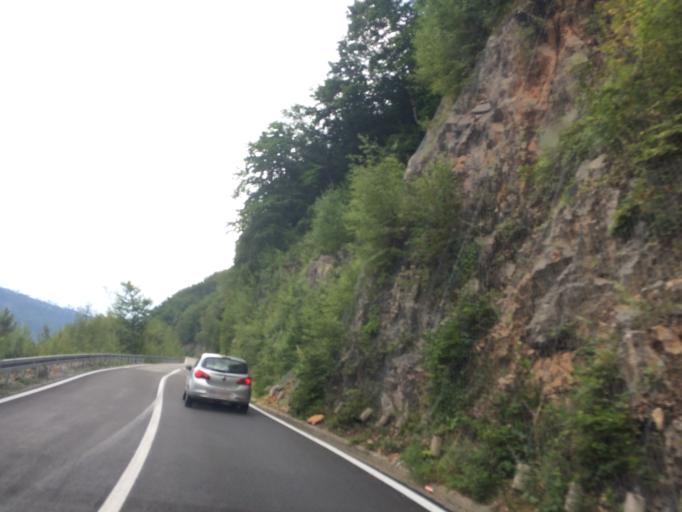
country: ME
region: Opstina Zabljak
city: Zabljak
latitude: 43.1516
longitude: 19.2777
